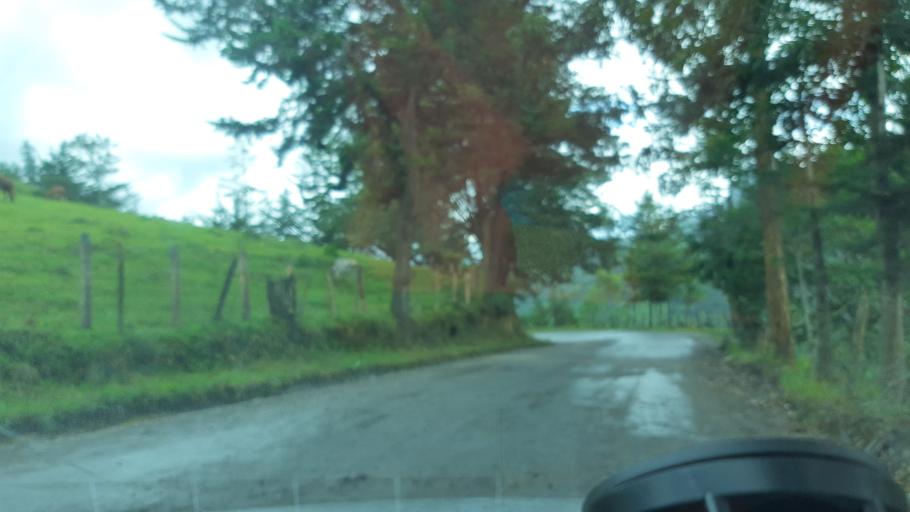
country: CO
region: Boyaca
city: Chinavita
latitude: 5.1571
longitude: -73.3690
